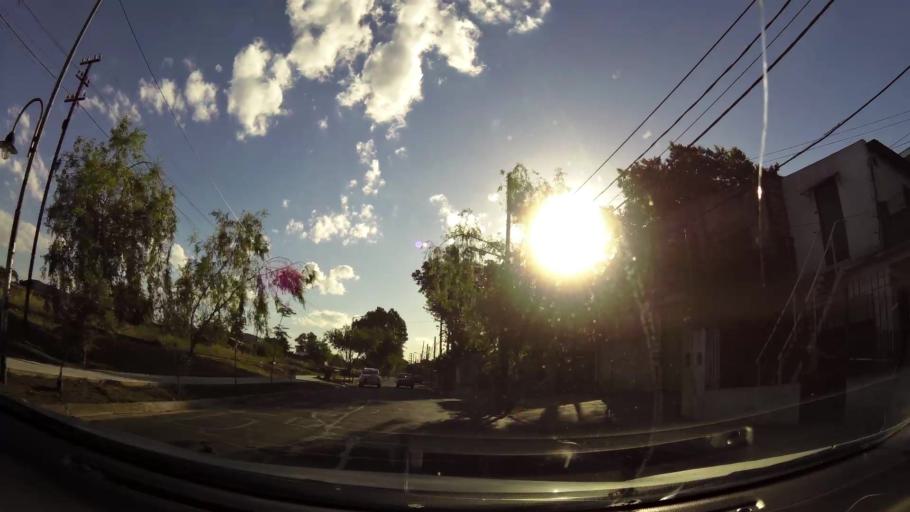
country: AR
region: Buenos Aires
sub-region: Partido de San Isidro
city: San Isidro
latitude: -34.4604
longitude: -58.5507
